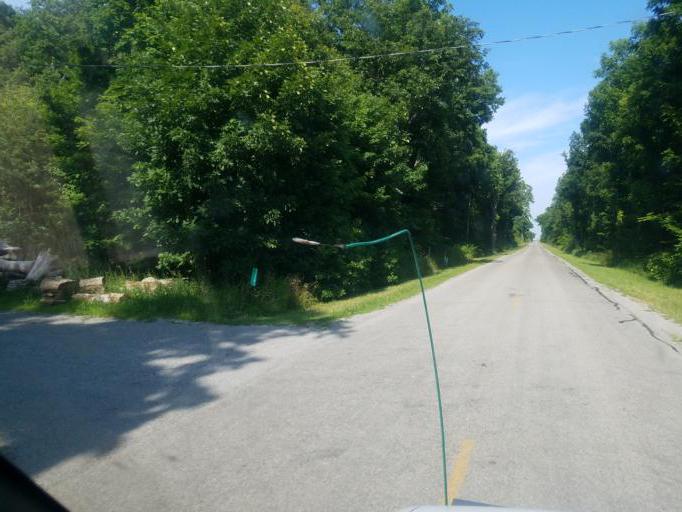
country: US
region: Ohio
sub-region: Hardin County
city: Kenton
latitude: 40.5558
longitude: -83.6304
